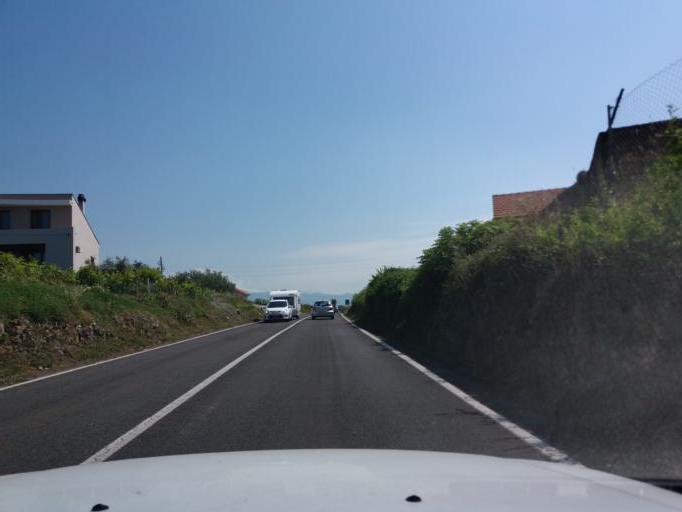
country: HR
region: Zadarska
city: Policnik
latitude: 44.1471
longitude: 15.3238
